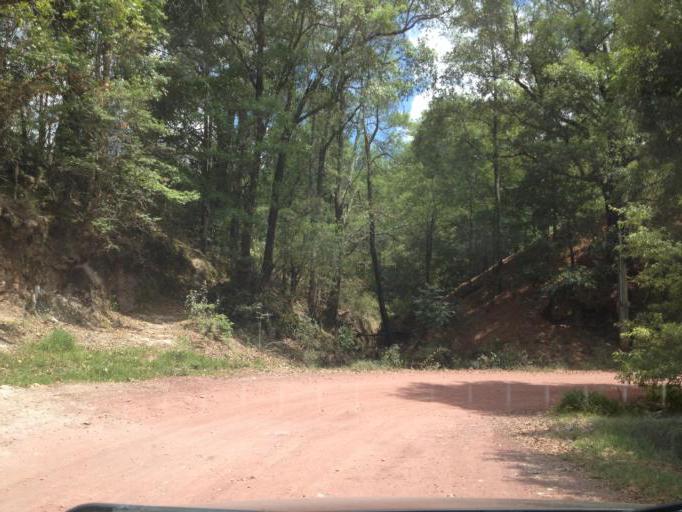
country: MX
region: Hidalgo
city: Mineral del Monte
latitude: 20.2065
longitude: -98.6578
